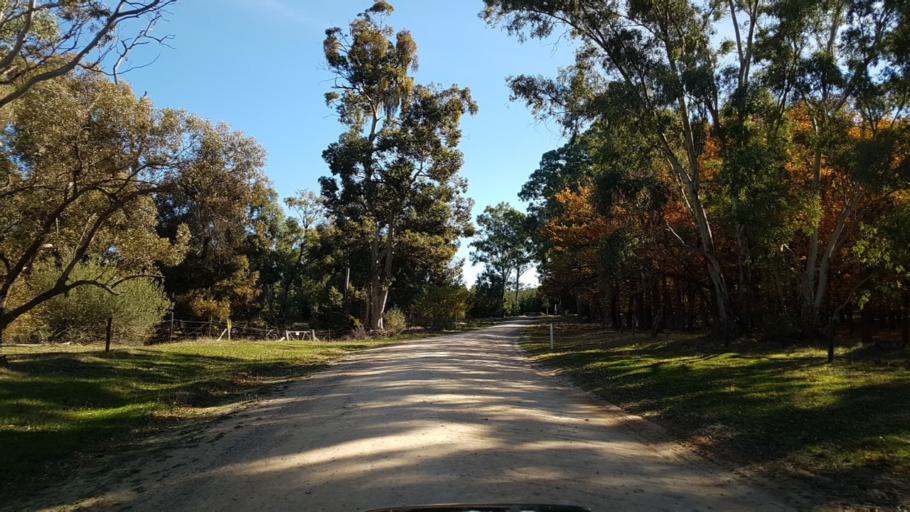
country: AU
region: South Australia
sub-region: Northern Areas
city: Jamestown
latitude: -33.2859
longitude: 138.5627
